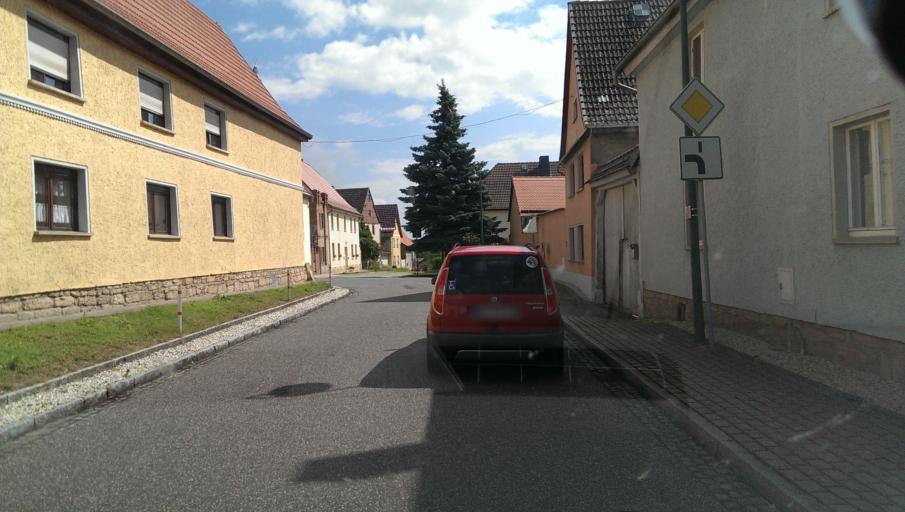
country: DE
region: Saxony-Anhalt
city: Eckartsberga
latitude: 51.1564
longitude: 11.5662
